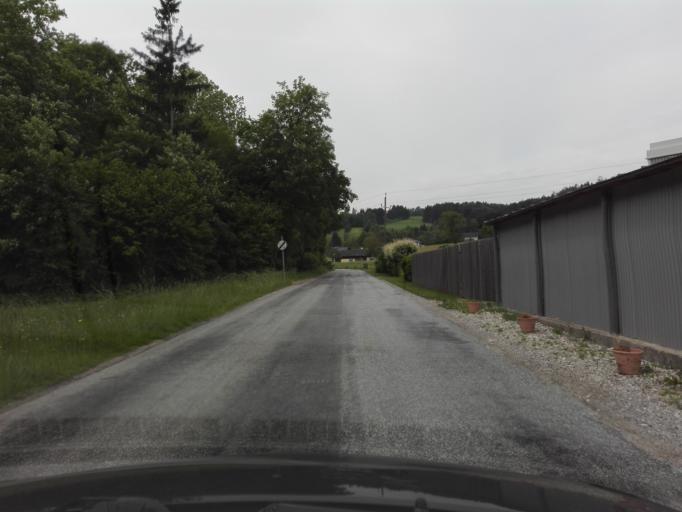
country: AT
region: Upper Austria
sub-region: Politischer Bezirk Gmunden
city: Scharnstein
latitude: 47.9265
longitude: 13.9897
